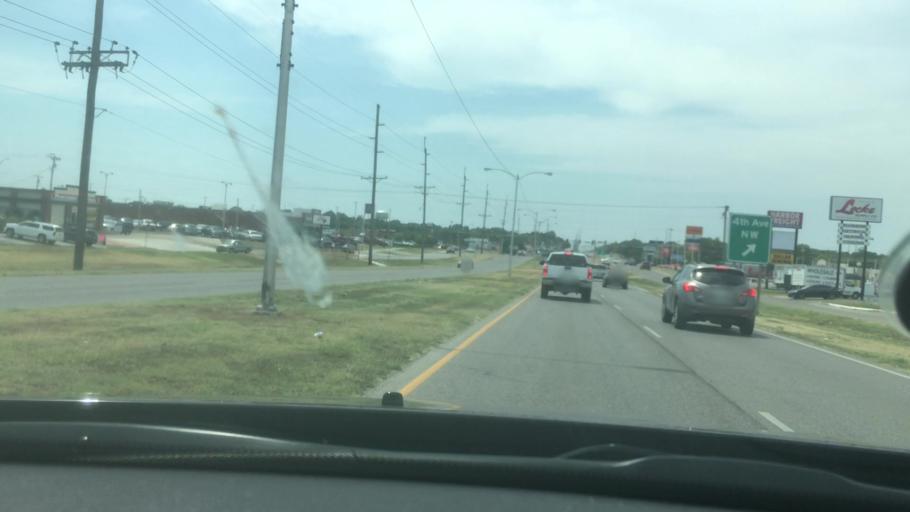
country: US
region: Oklahoma
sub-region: Carter County
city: Ardmore
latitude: 34.1829
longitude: -97.1431
